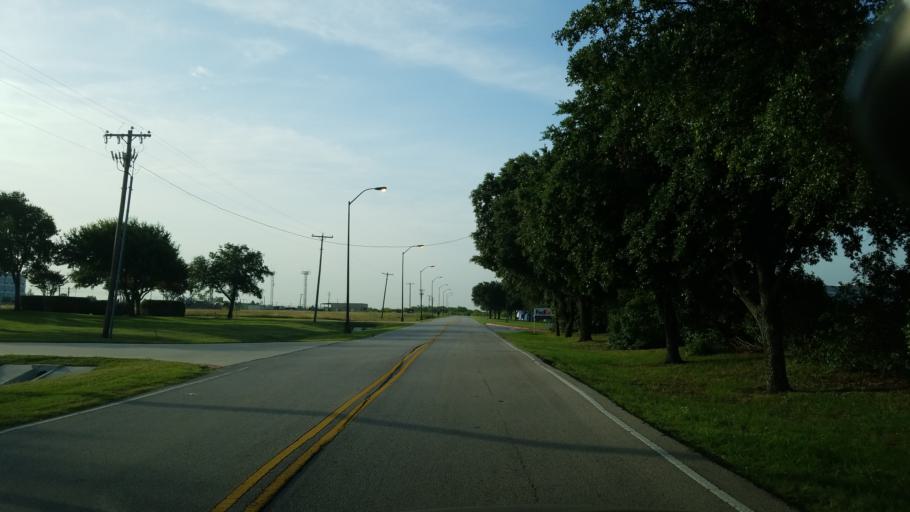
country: US
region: Texas
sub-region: Dallas County
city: Coppell
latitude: 32.9151
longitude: -97.0177
